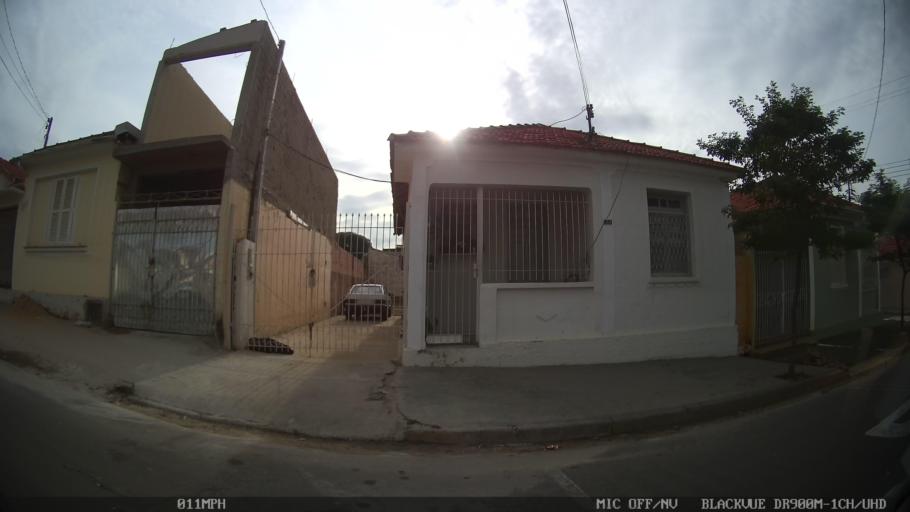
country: BR
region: Sao Paulo
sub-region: Piracicaba
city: Piracicaba
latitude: -22.7305
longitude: -47.6335
